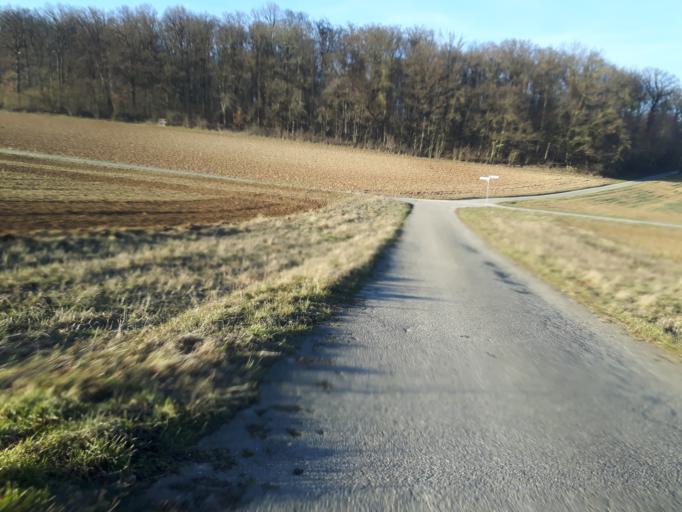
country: DE
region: Baden-Wuerttemberg
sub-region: Regierungsbezirk Stuttgart
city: Leingarten
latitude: 49.1605
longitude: 9.0969
